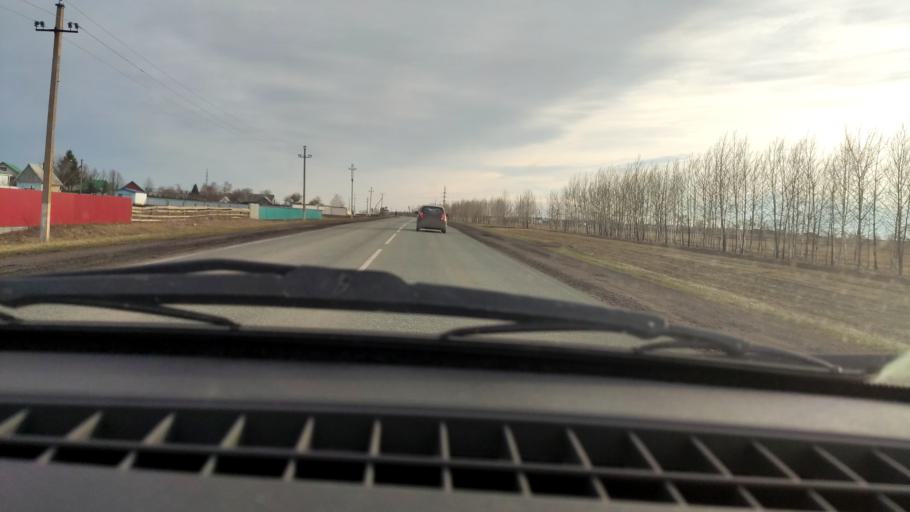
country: RU
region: Bashkortostan
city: Davlekanovo
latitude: 54.3877
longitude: 55.1999
